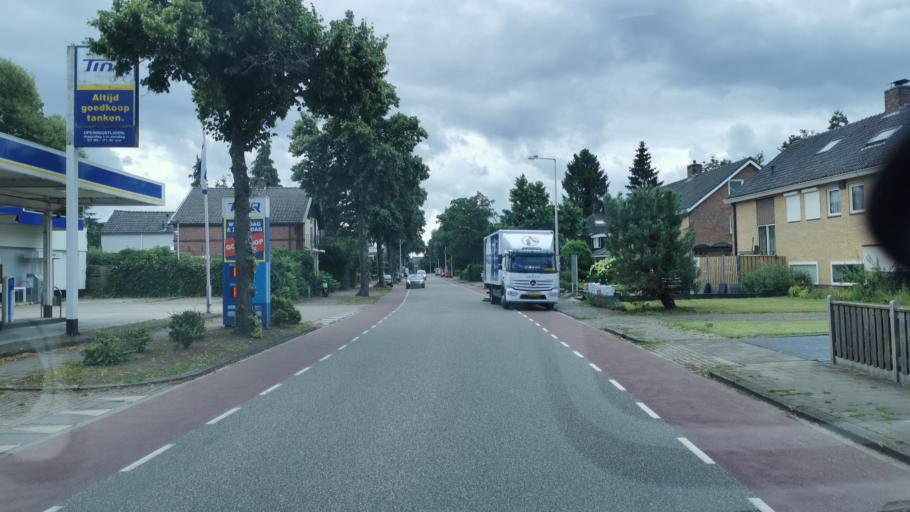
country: NL
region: Overijssel
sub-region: Gemeente Enschede
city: Enschede
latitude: 52.2371
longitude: 6.8846
